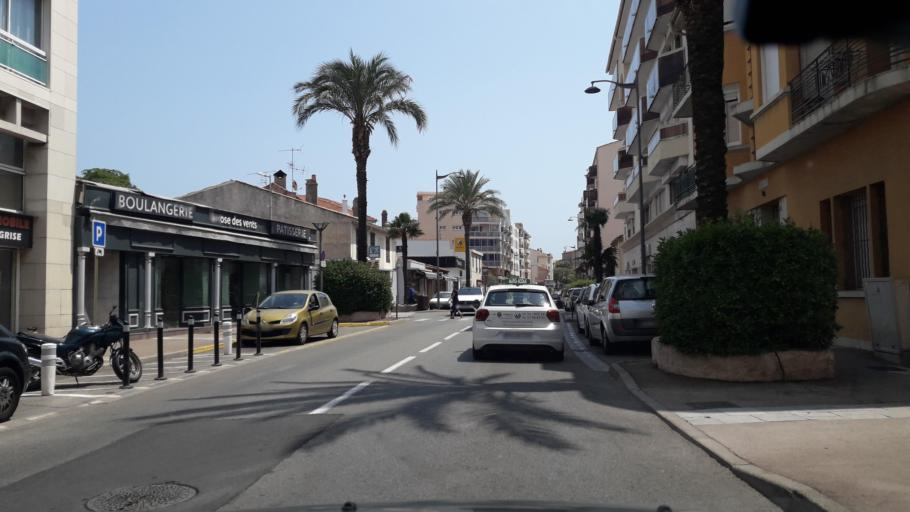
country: FR
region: Provence-Alpes-Cote d'Azur
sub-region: Departement du Var
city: Saint-Raphael
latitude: 43.4281
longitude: 6.7657
